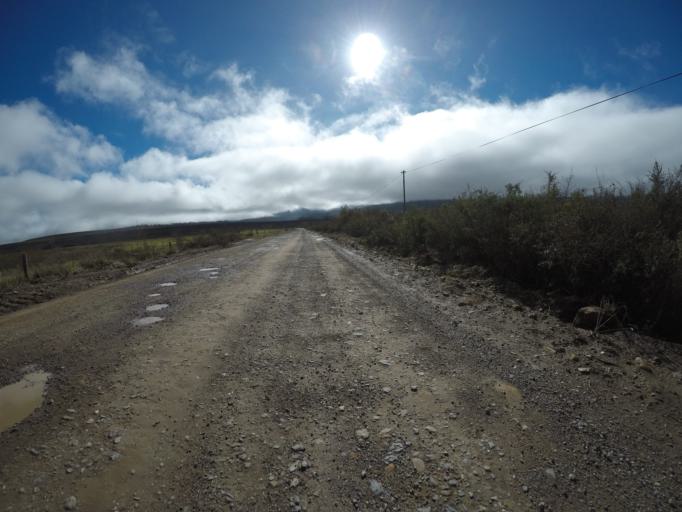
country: ZA
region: Western Cape
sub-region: Cape Winelands District Municipality
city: Ashton
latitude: -34.1253
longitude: 19.8396
